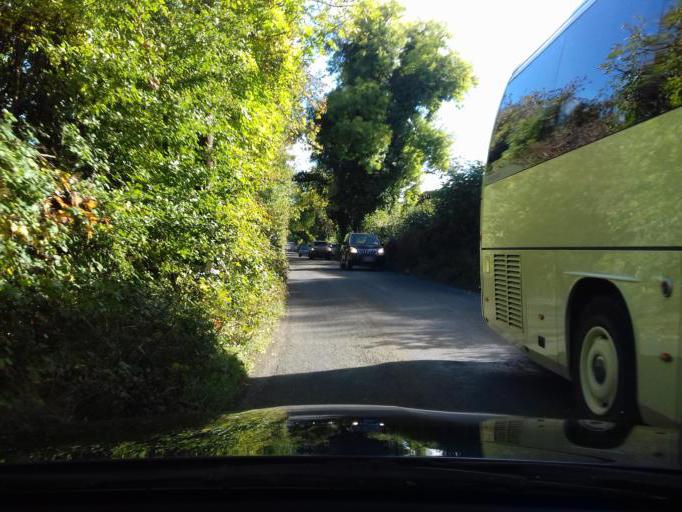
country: IE
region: Leinster
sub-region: An Mhi
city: Slane
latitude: 53.6864
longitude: -6.4883
